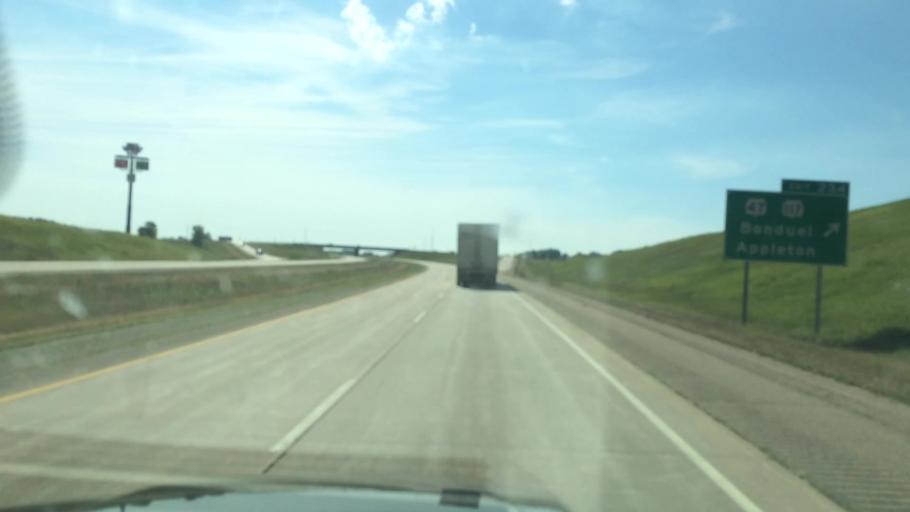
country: US
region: Wisconsin
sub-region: Shawano County
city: Bonduel
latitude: 44.7291
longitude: -88.4528
